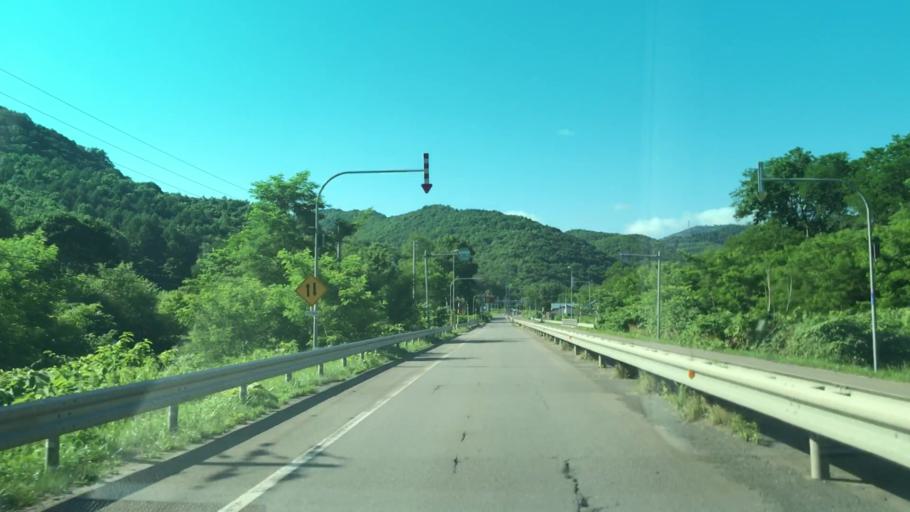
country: JP
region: Hokkaido
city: Iwanai
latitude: 43.0033
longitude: 140.6679
